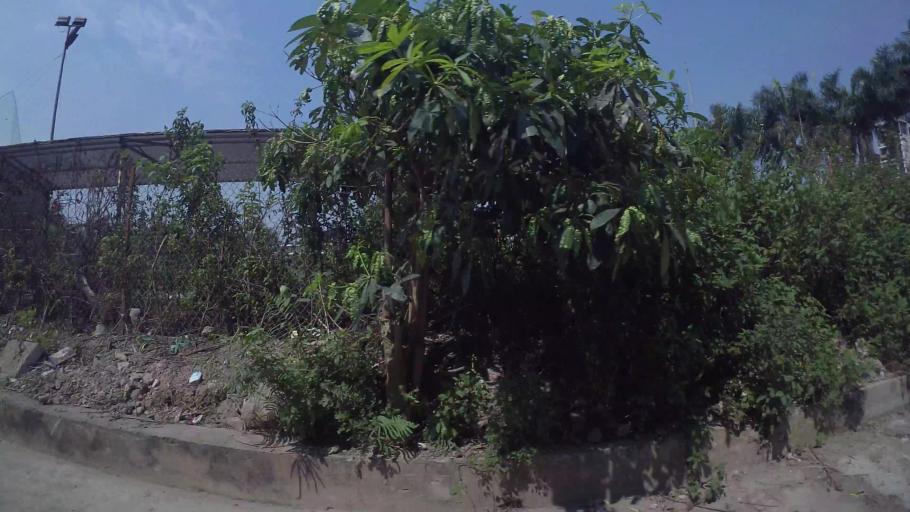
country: VN
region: Ha Noi
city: Hoan Kiem
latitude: 21.0627
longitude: 105.8700
